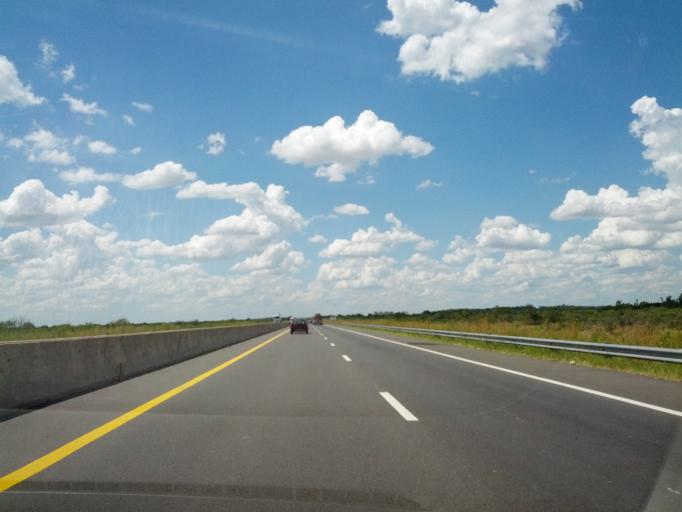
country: AR
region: Entre Rios
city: Colonia Elia
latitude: -32.7554
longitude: -58.4877
